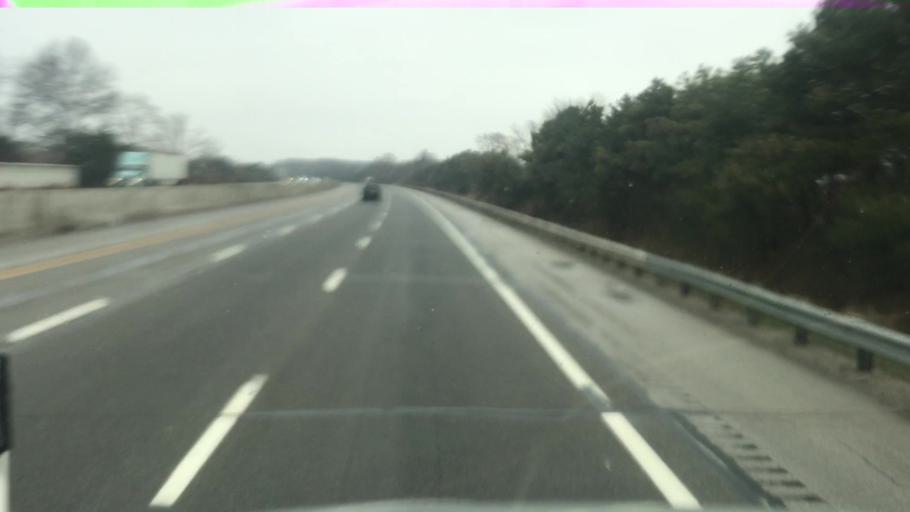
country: US
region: Ohio
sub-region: Cuyahoga County
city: Berea
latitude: 41.3539
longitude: -81.8735
